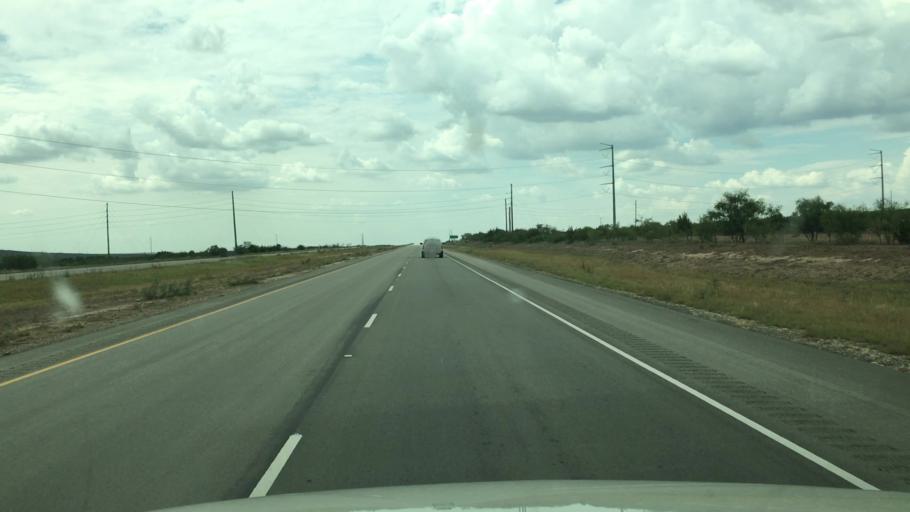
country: US
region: Texas
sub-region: Glasscock County
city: Garden City
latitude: 31.9869
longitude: -101.2630
